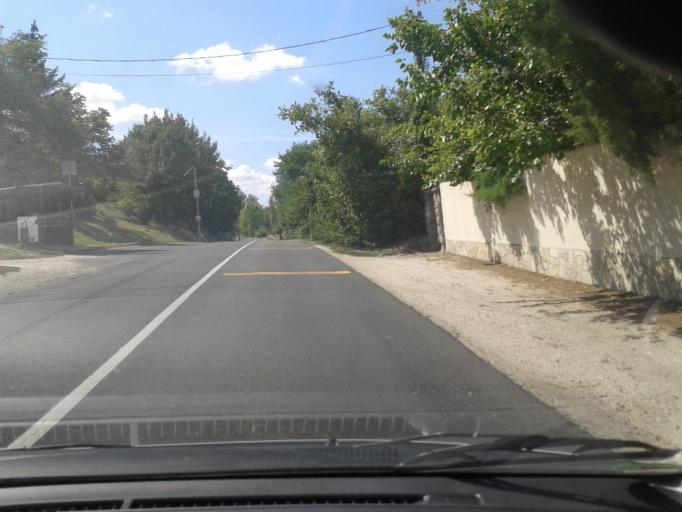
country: HU
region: Pest
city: Szob
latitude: 47.8140
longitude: 18.8089
